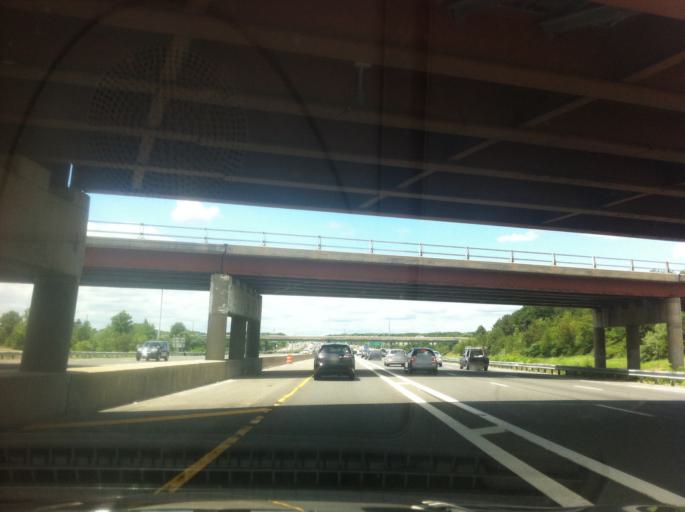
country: US
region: New York
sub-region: Suffolk County
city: Commack
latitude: 40.8049
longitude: -73.2807
